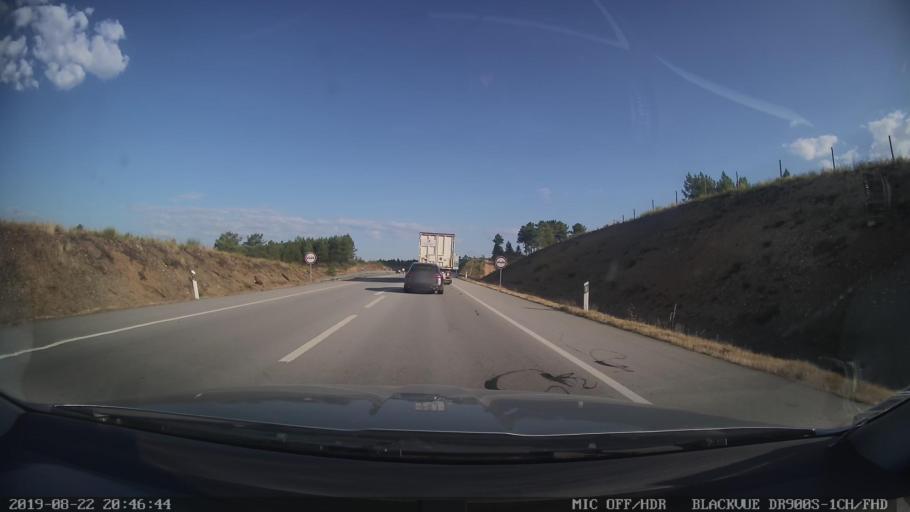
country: PT
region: Castelo Branco
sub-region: Proenca-A-Nova
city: Proenca-a-Nova
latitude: 39.7290
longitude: -7.8790
